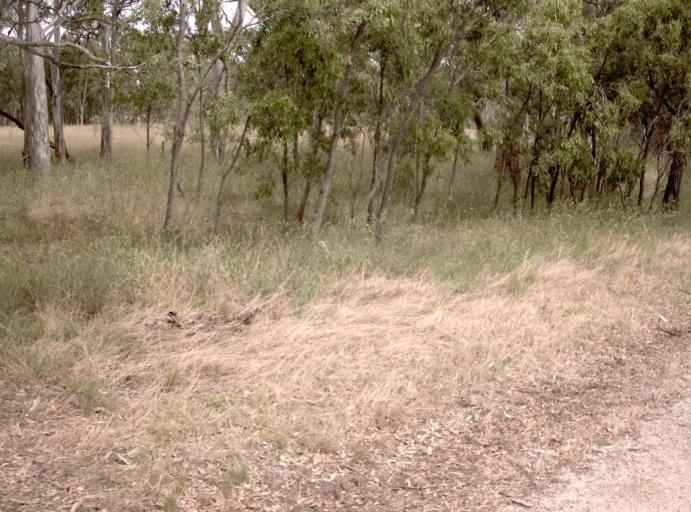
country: AU
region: Victoria
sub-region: Wellington
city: Sale
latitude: -37.9105
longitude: 147.0804
